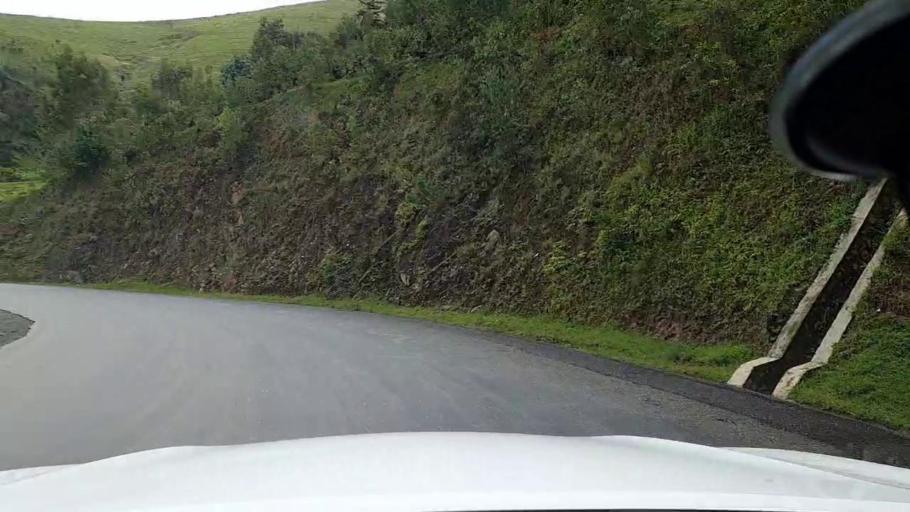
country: RW
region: Southern Province
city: Gitarama
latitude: -2.0610
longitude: 29.5614
